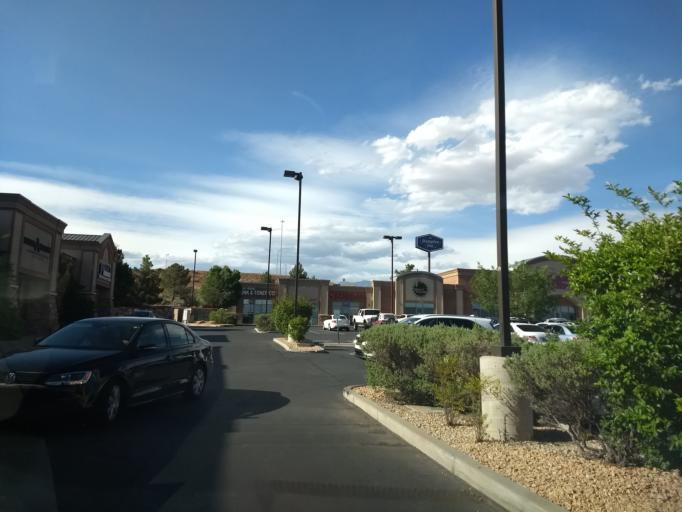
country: US
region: Utah
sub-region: Washington County
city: Saint George
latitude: 37.1073
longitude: -113.5569
